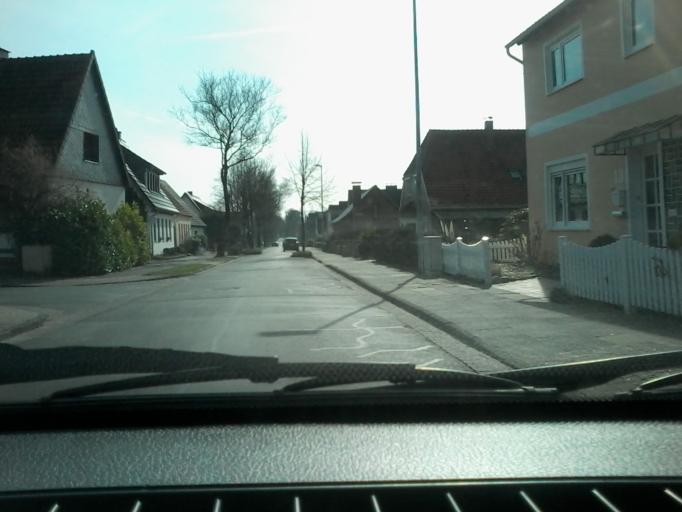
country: DE
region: Lower Saxony
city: Achim
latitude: 53.0088
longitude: 9.0359
